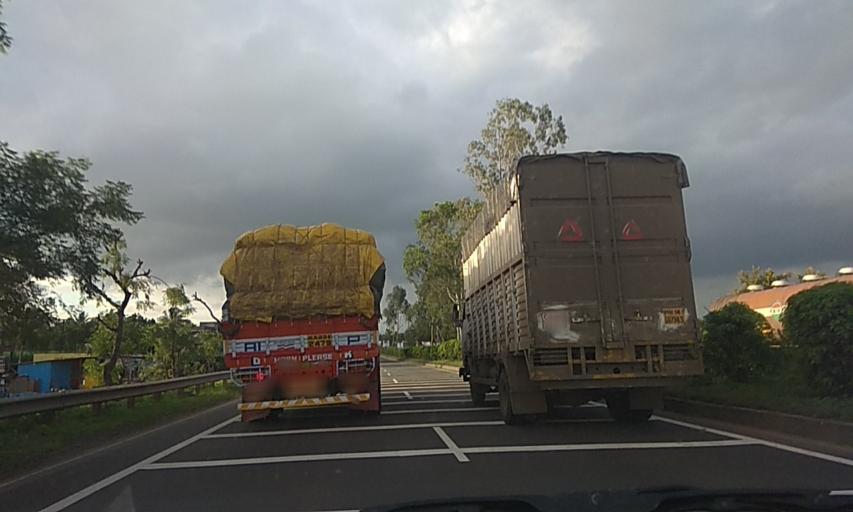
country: IN
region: Maharashtra
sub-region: Satara Division
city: Rahimatpur
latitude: 17.4811
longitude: 74.0855
